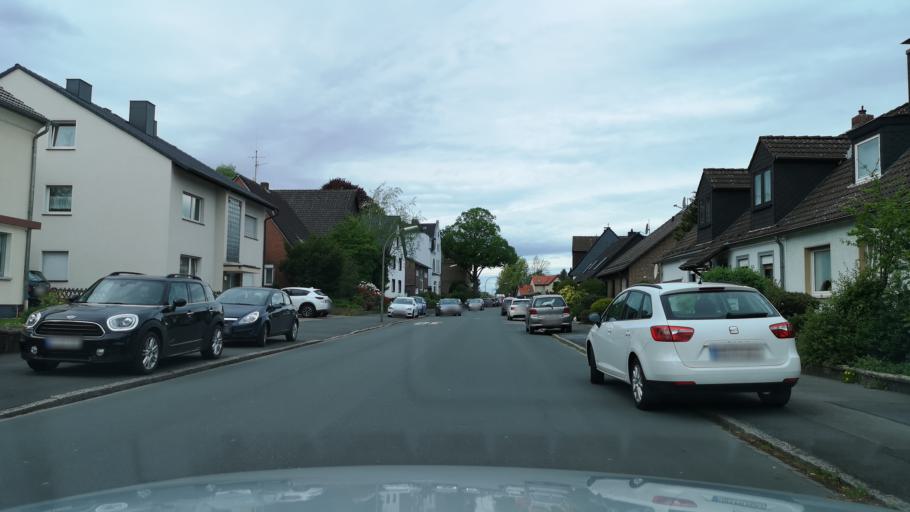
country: DE
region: North Rhine-Westphalia
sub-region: Regierungsbezirk Arnsberg
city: Holzwickede
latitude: 51.4954
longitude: 7.5910
